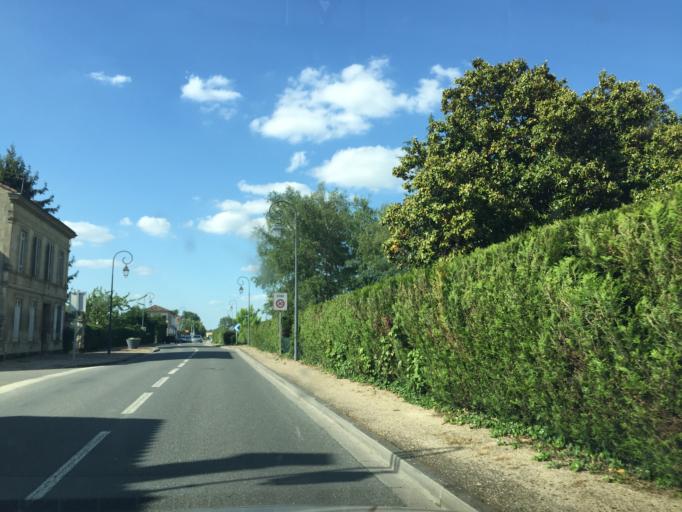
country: FR
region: Aquitaine
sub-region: Departement de la Gironde
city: Sainte-Terre
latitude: 44.8210
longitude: -0.1353
